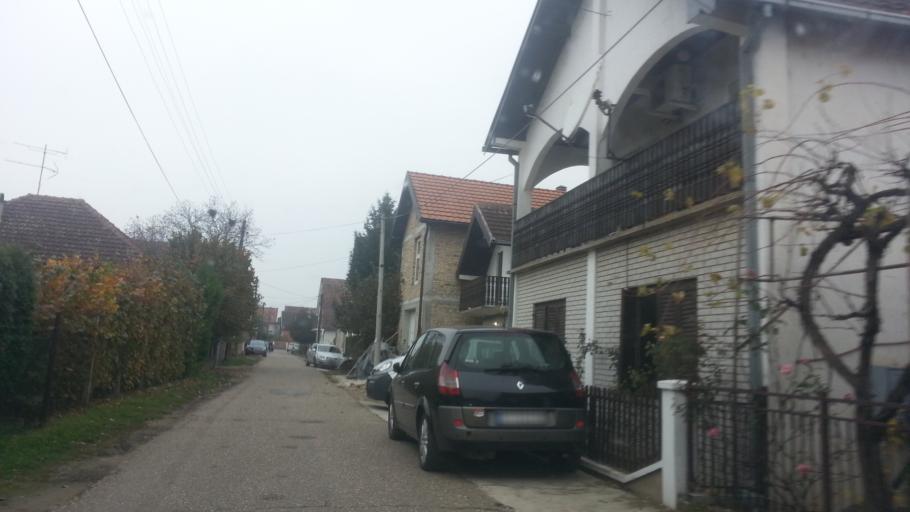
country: RS
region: Autonomna Pokrajina Vojvodina
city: Nova Pazova
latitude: 44.9533
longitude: 20.2193
